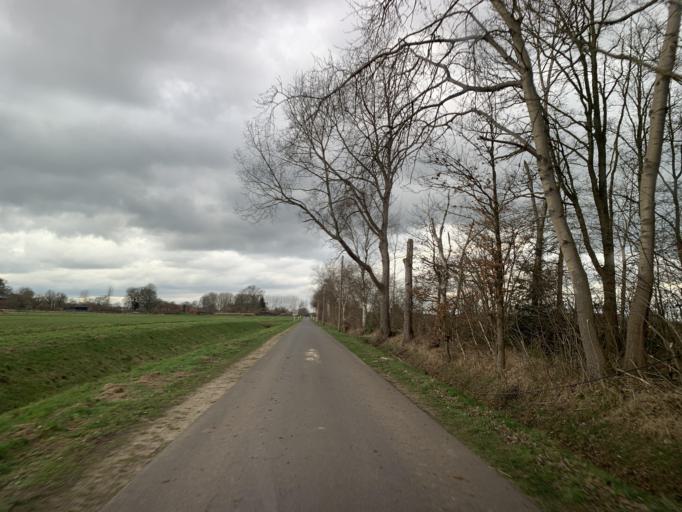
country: DE
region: North Rhine-Westphalia
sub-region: Regierungsbezirk Munster
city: Muenster
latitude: 52.0289
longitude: 7.6351
